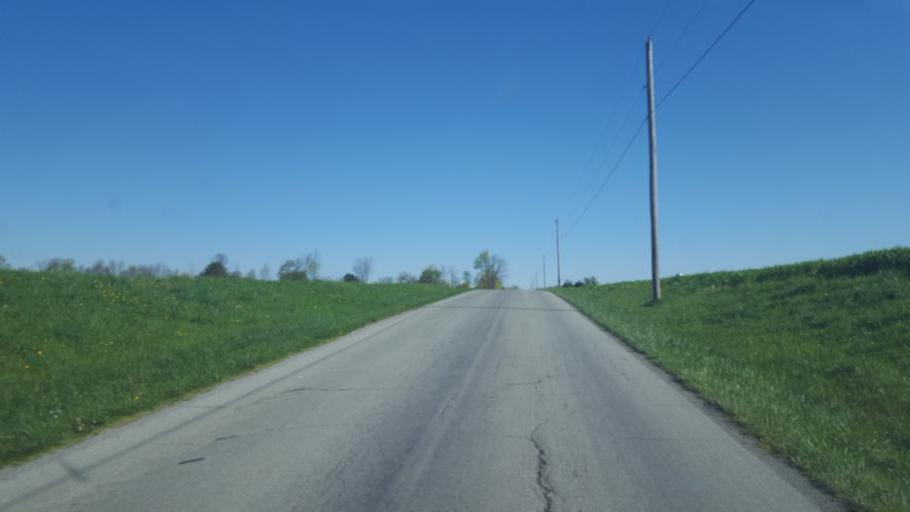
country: US
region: Ohio
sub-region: Wyandot County
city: Upper Sandusky
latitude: 40.8818
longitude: -83.2227
